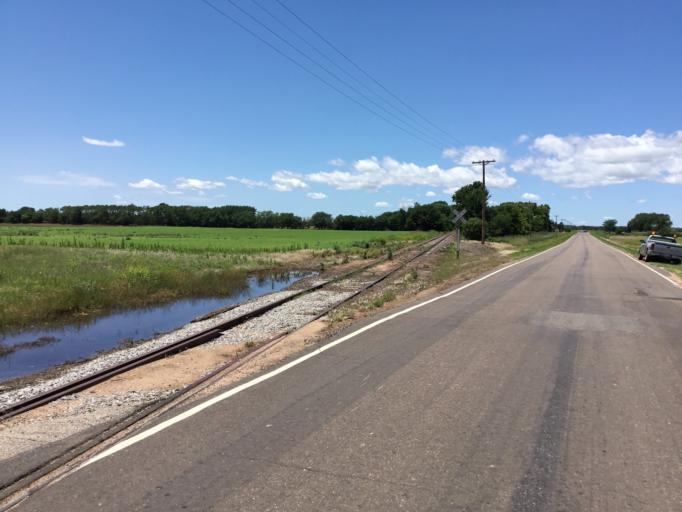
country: US
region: Kansas
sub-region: Sedgwick County
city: Cheney
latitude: 37.6186
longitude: -97.8496
